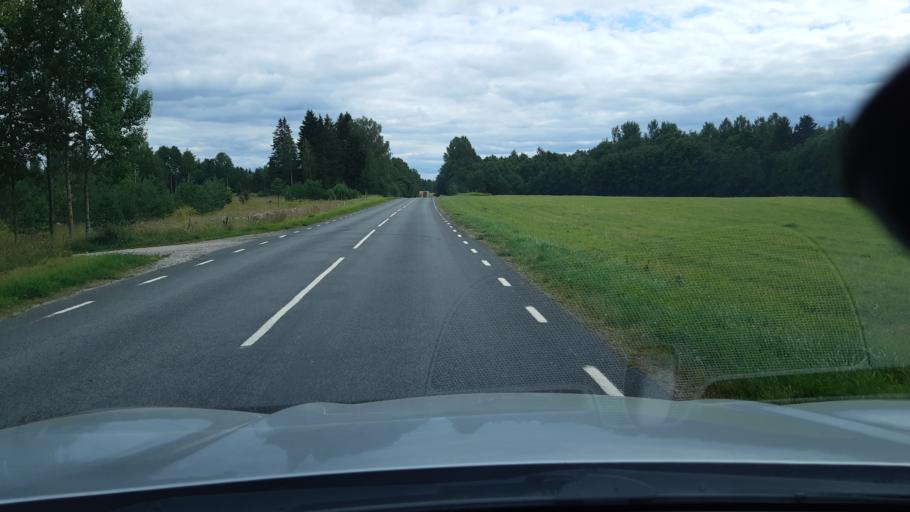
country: EE
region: Raplamaa
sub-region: Maerjamaa vald
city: Marjamaa
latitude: 59.0447
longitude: 24.4814
